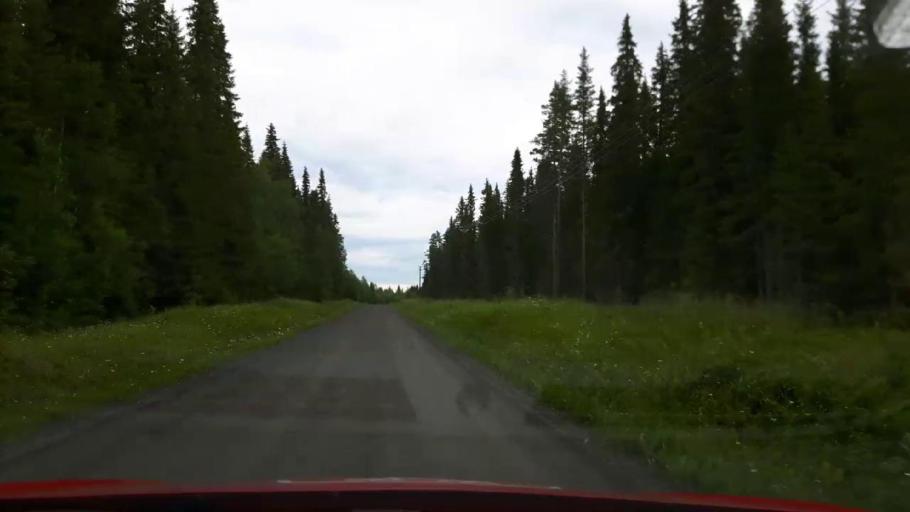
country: SE
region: Jaemtland
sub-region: Stroemsunds Kommun
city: Stroemsund
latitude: 63.4669
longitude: 15.2857
